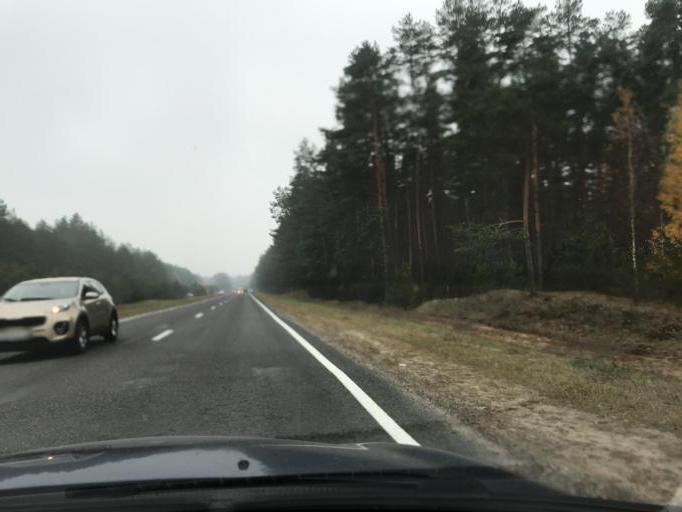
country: LT
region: Alytaus apskritis
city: Druskininkai
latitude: 53.8553
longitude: 23.8918
